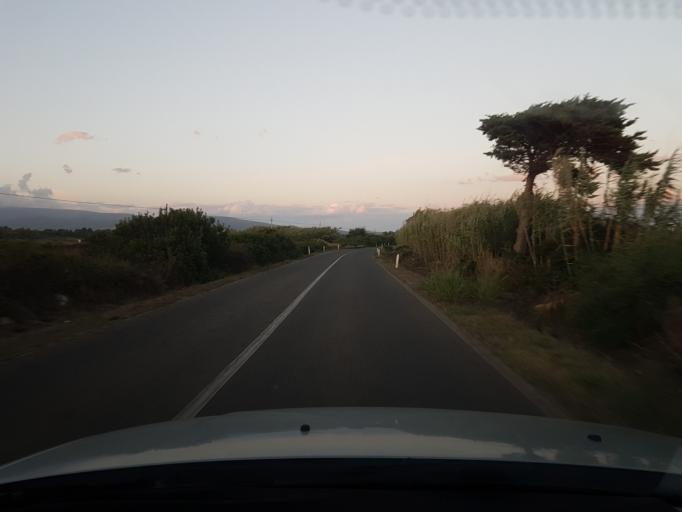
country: IT
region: Sardinia
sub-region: Provincia di Oristano
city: Riola Sardo
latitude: 40.0217
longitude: 8.4618
